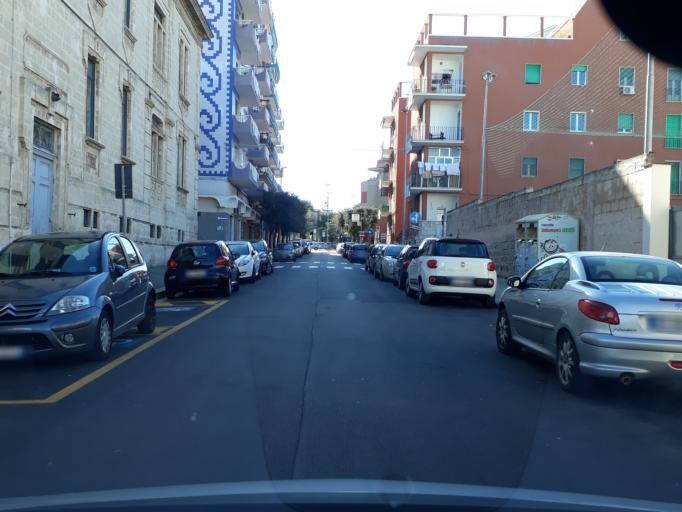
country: IT
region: Apulia
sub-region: Provincia di Bari
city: Monopoli
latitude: 40.9525
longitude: 17.2947
